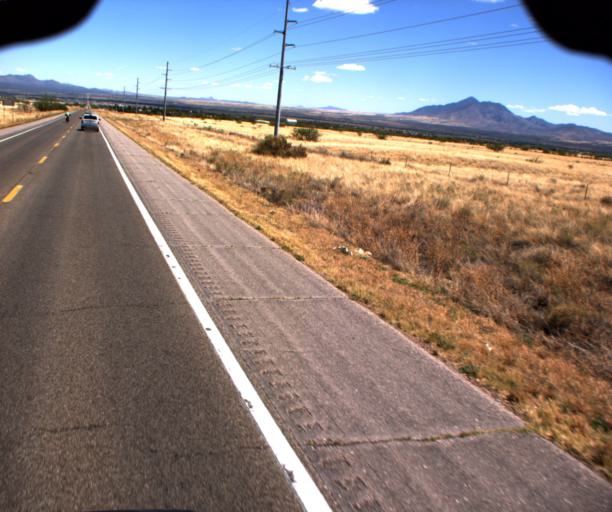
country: US
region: Arizona
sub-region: Cochise County
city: Sierra Vista Southeast
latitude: 31.3799
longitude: -110.1998
